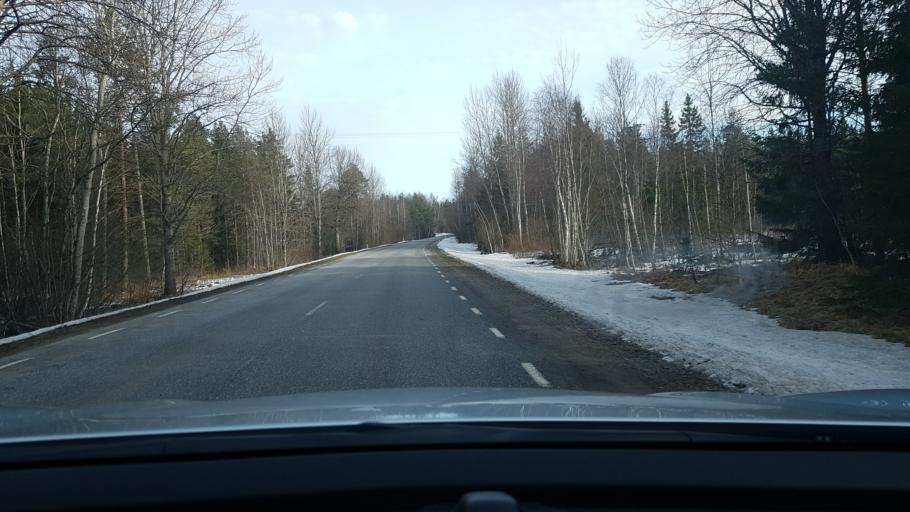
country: EE
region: Saare
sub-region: Kuressaare linn
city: Kuressaare
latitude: 58.4224
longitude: 22.6681
